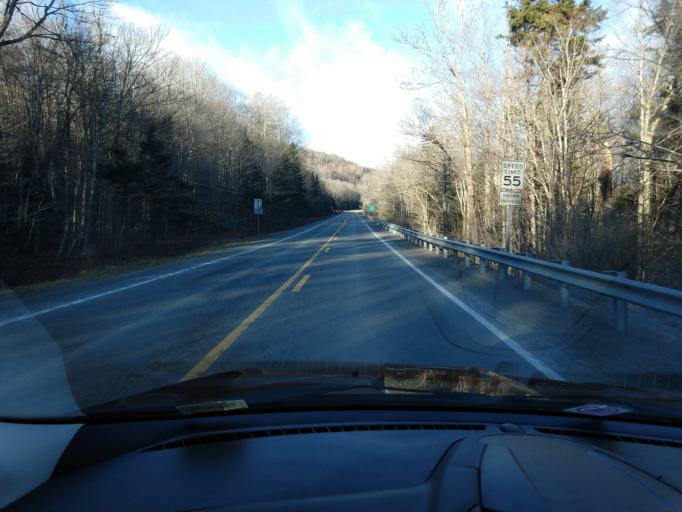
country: US
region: West Virginia
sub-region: Randolph County
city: Elkins
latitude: 38.6002
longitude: -79.8517
